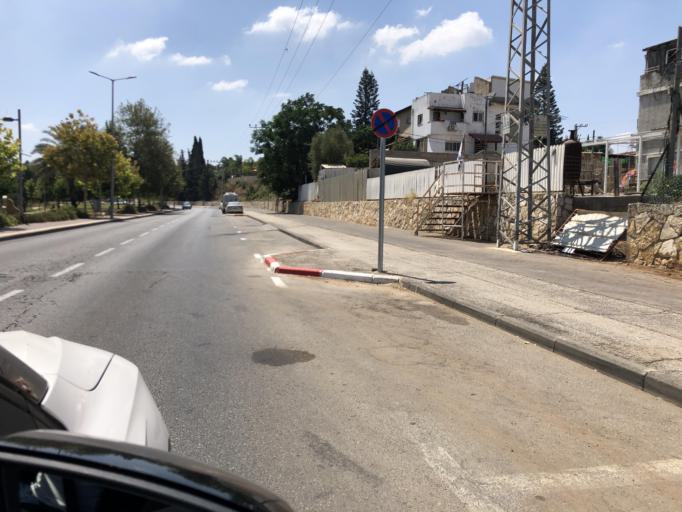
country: IL
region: Central District
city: Rosh Ha'Ayin
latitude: 32.0998
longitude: 34.9568
